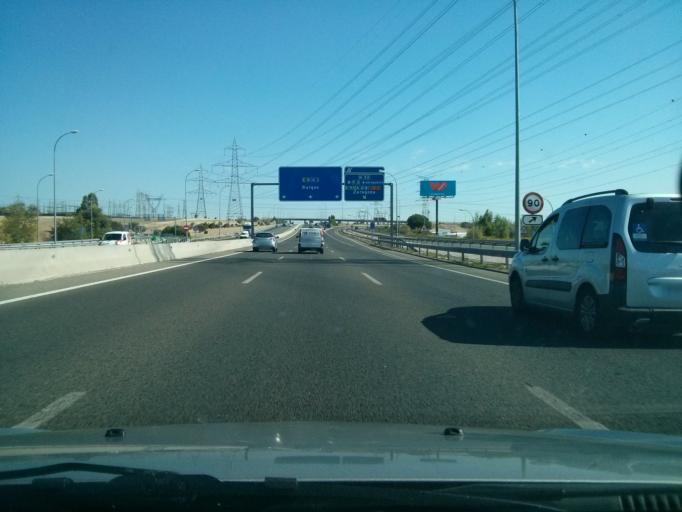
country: ES
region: Madrid
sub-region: Provincia de Madrid
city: San Sebastian de los Reyes
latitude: 40.5581
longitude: -3.6008
